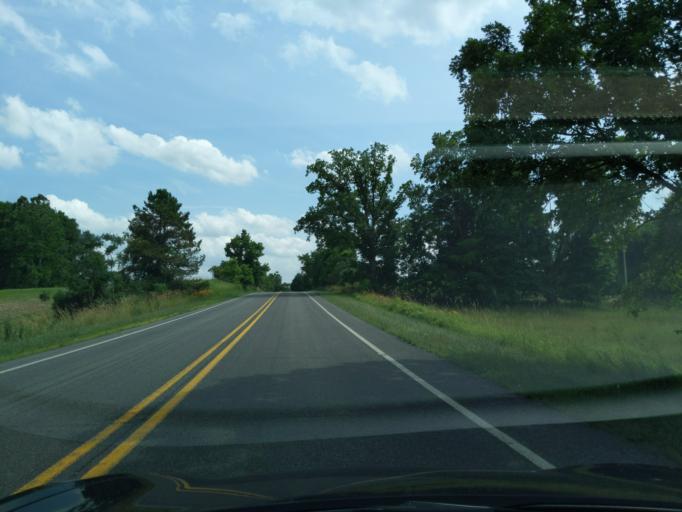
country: US
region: Michigan
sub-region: Eaton County
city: Dimondale
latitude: 42.5938
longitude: -84.6025
